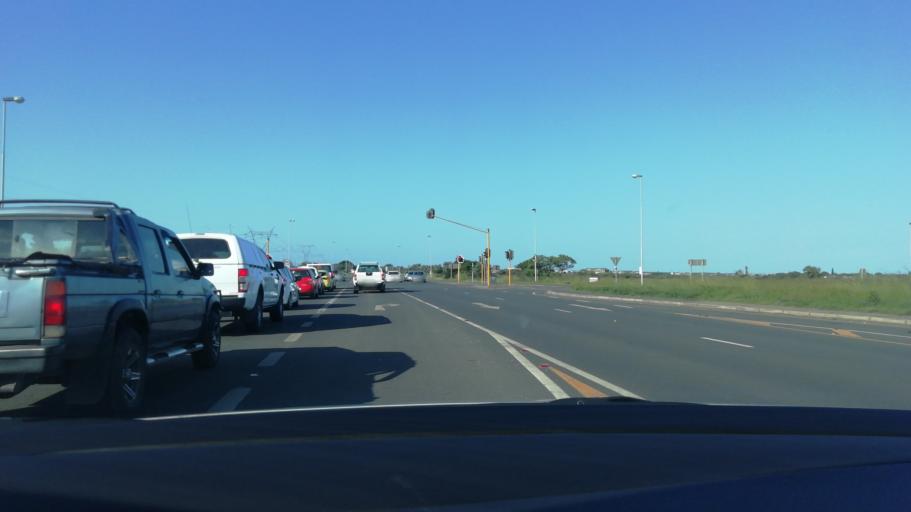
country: ZA
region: KwaZulu-Natal
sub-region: uThungulu District Municipality
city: Richards Bay
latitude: -28.7690
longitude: 32.0353
